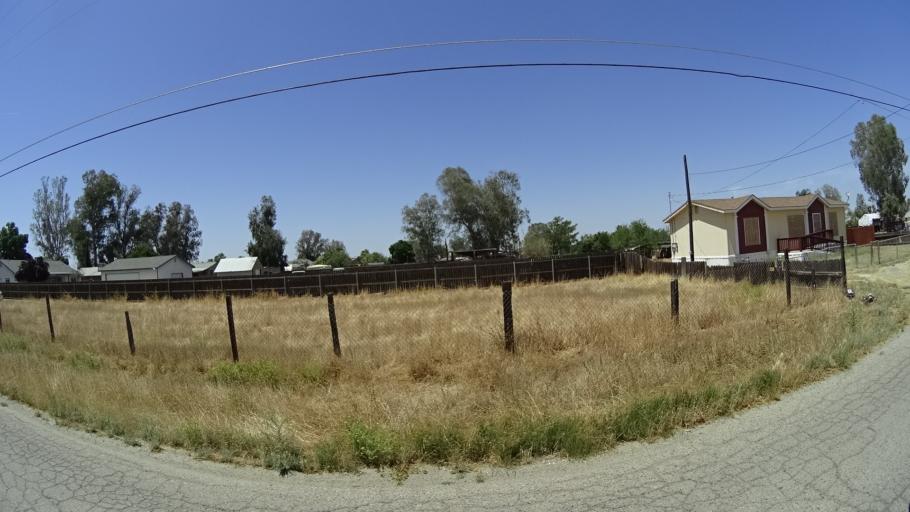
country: US
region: California
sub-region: Kings County
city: Corcoran
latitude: 36.1171
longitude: -119.5767
